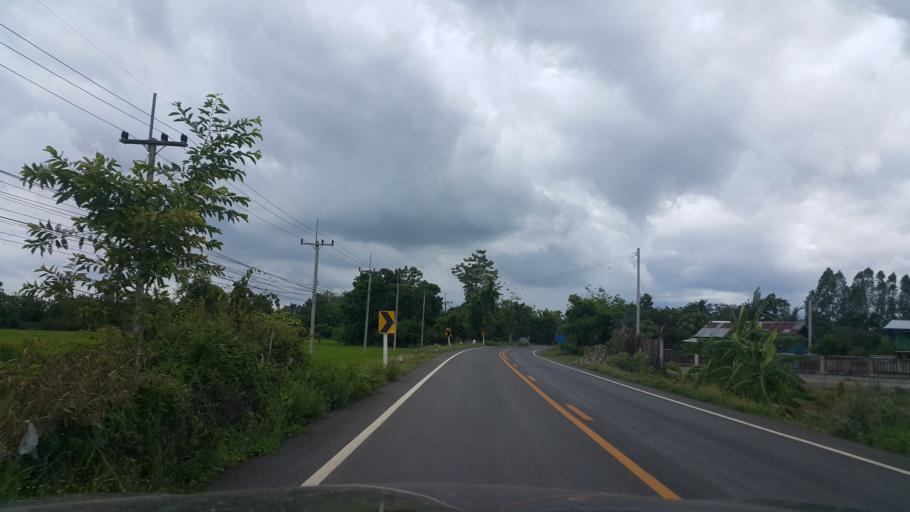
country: TH
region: Sukhothai
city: Sukhothai
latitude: 16.9157
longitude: 99.8688
